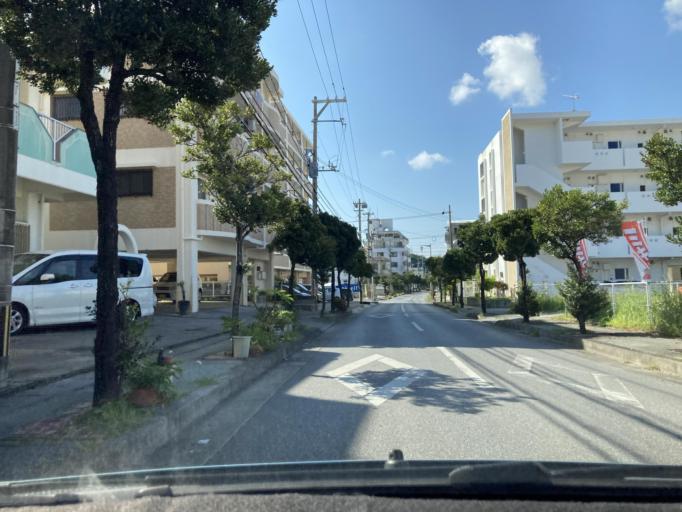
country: JP
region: Okinawa
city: Tomigusuku
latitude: 26.1801
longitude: 127.6561
